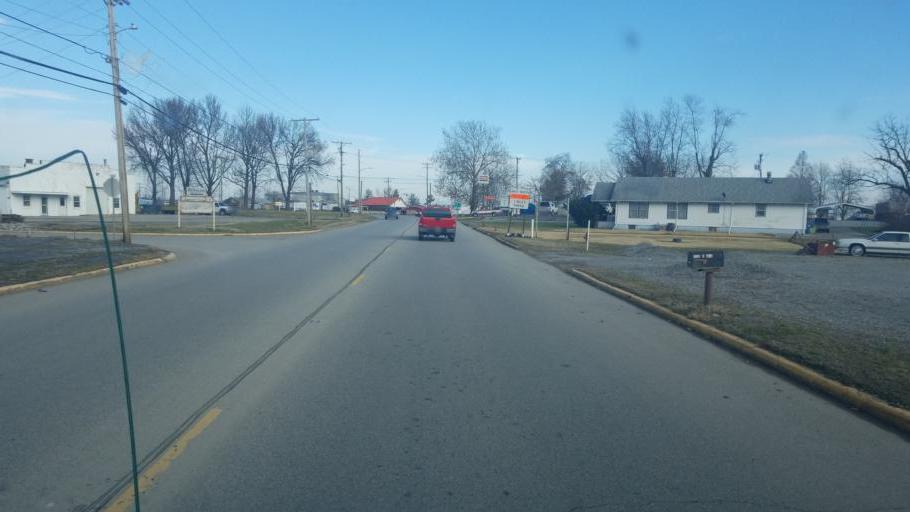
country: US
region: Illinois
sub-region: White County
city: Carmi
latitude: 38.0969
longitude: -88.1482
